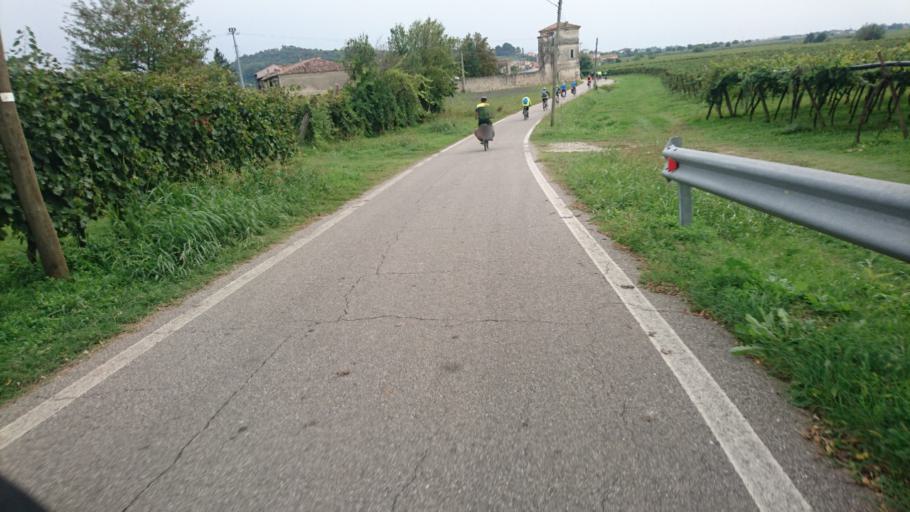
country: IT
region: Veneto
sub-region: Provincia di Verona
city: Colognola ai Colli
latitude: 45.4210
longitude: 11.2042
